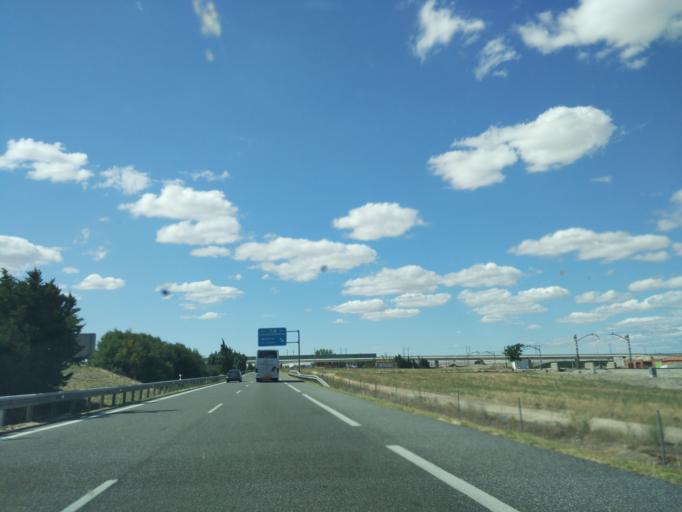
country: ES
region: Castille and Leon
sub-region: Provincia de Valladolid
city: Medina del Campo
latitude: 41.2843
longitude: -4.8951
